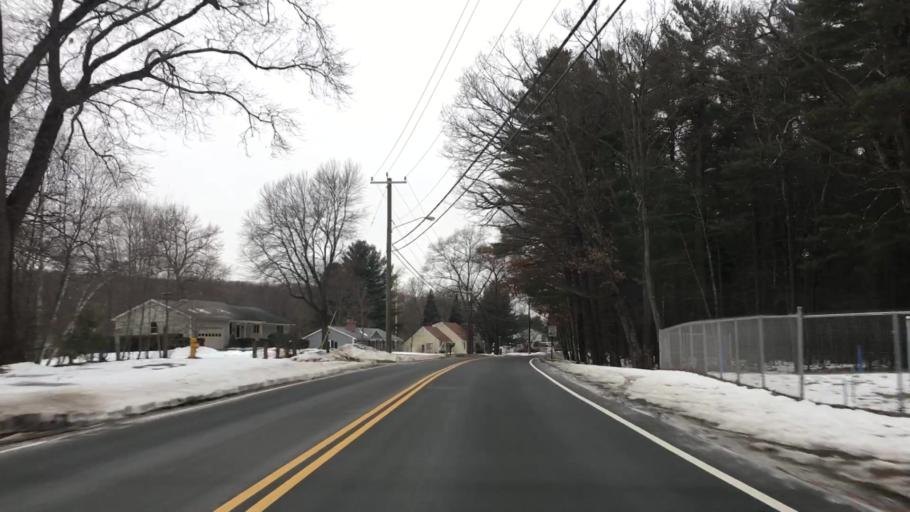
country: US
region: Massachusetts
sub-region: Hampden County
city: West Springfield
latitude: 42.0998
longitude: -72.6868
